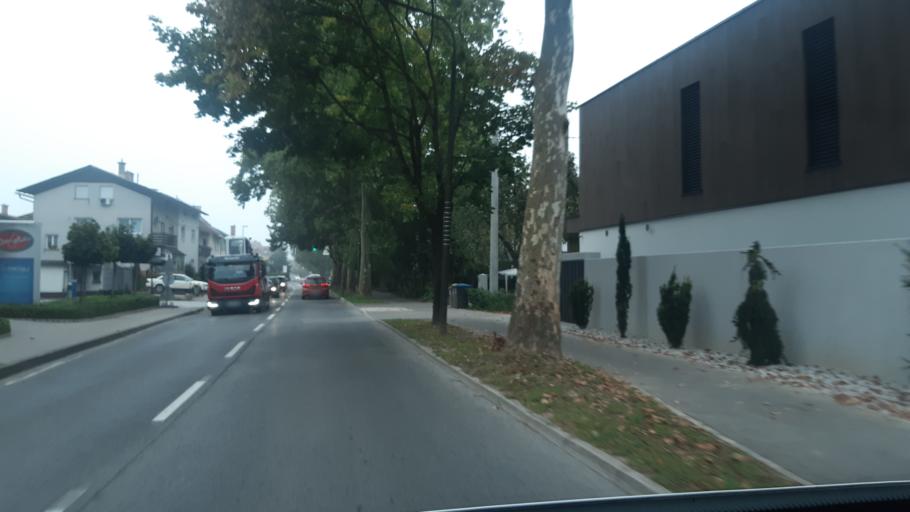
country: SI
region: Ljubljana
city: Ljubljana
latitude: 46.0719
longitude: 14.4681
